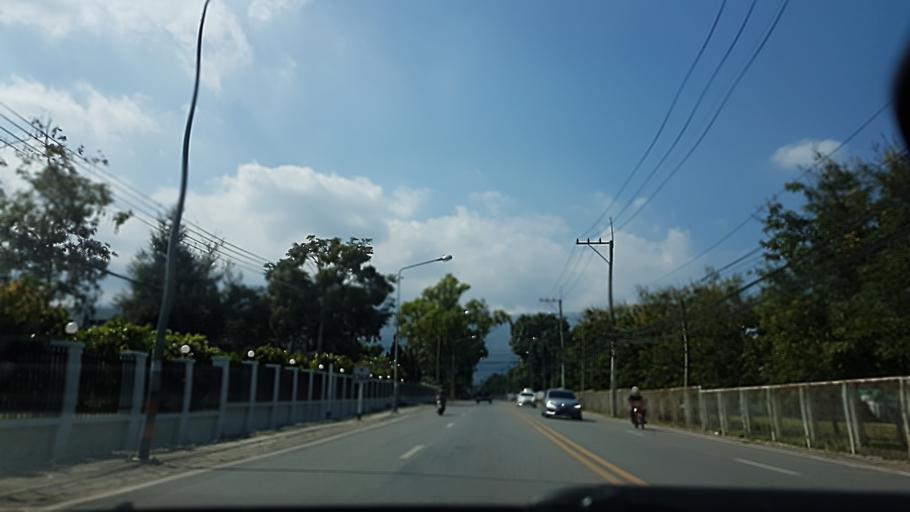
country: TH
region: Chiang Mai
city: Chiang Mai
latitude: 18.8176
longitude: 98.9802
